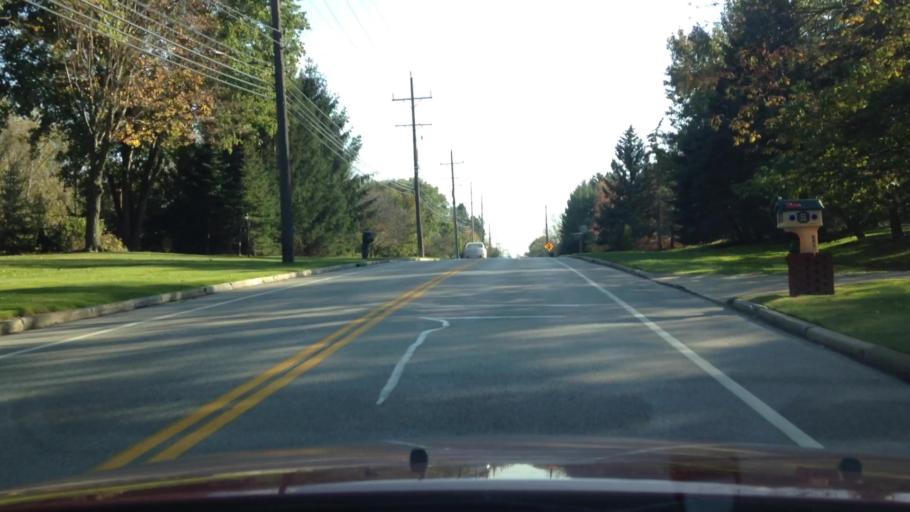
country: US
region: Ohio
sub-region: Cuyahoga County
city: Pepper Pike
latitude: 41.4695
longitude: -81.4635
